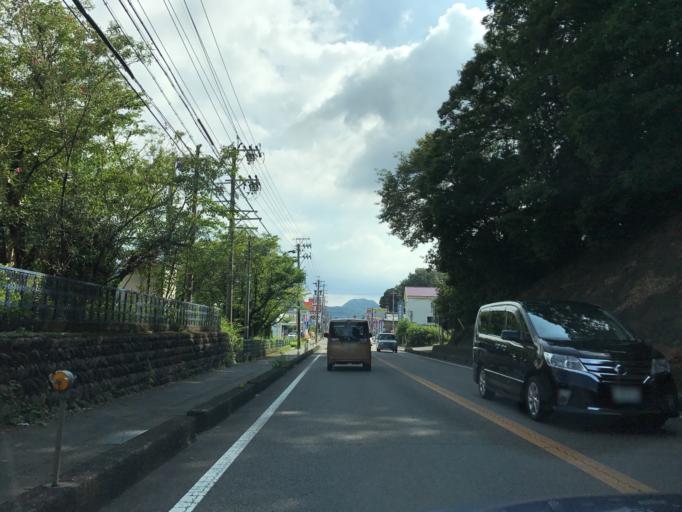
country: JP
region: Gifu
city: Kakamigahara
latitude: 35.4623
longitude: 136.8545
